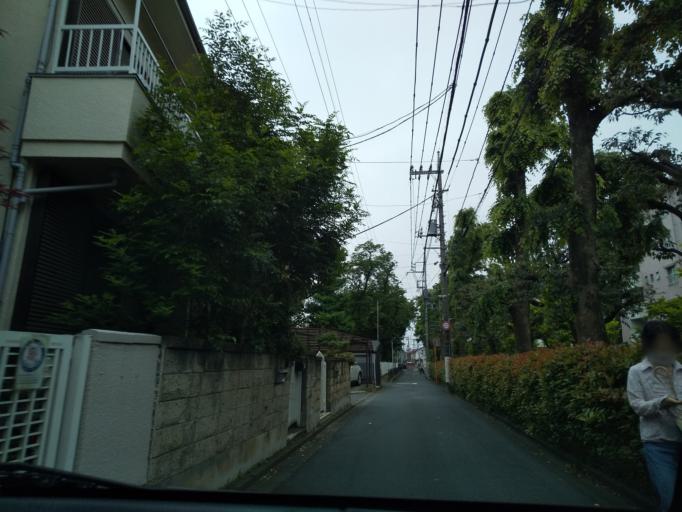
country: JP
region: Tokyo
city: Kokubunji
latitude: 35.6866
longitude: 139.4511
